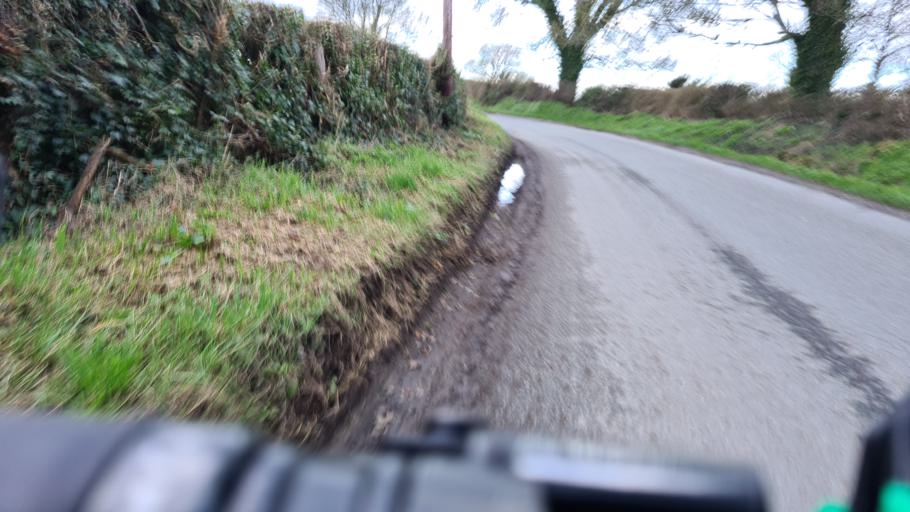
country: IE
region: Leinster
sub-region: Kildare
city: Maynooth
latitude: 53.3486
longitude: -6.5920
